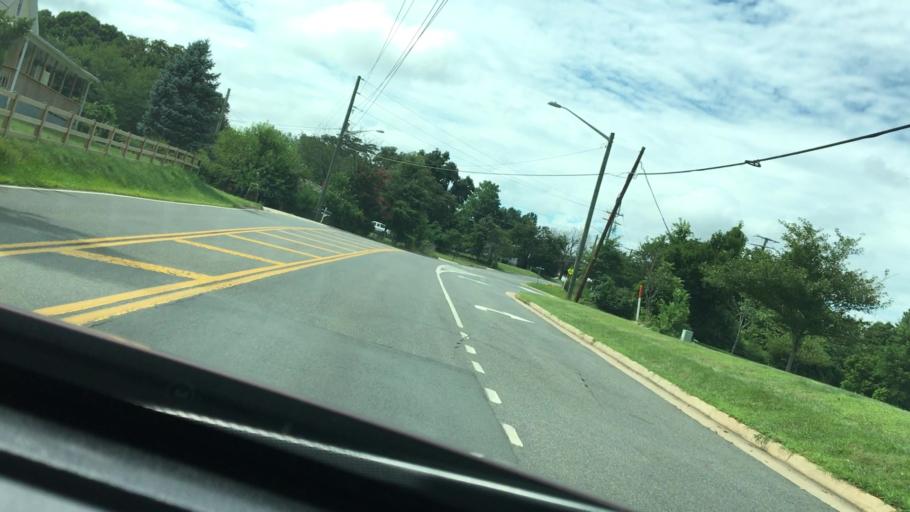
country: US
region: Virginia
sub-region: Prince William County
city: Buckhall
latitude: 38.7462
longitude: -77.4391
